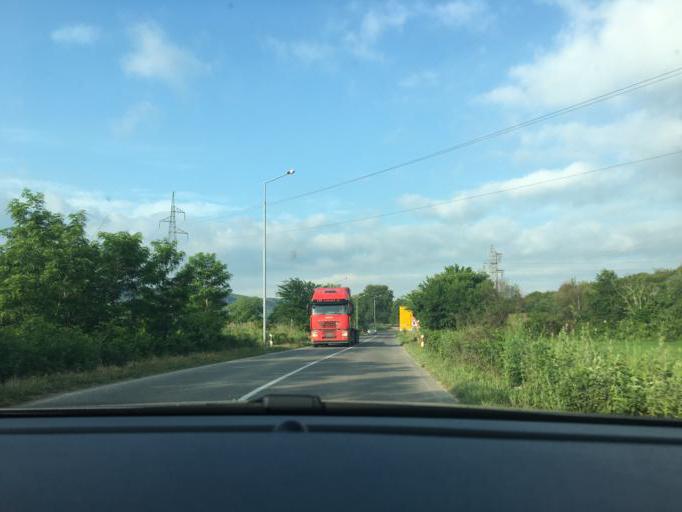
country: MK
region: Valandovo
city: Valandovo
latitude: 41.3073
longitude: 22.5444
